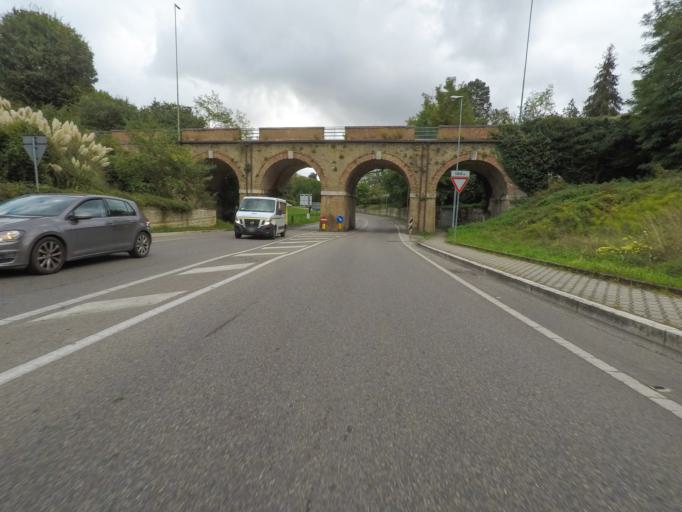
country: IT
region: Tuscany
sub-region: Provincia di Siena
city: Siena
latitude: 43.3275
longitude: 11.3388
